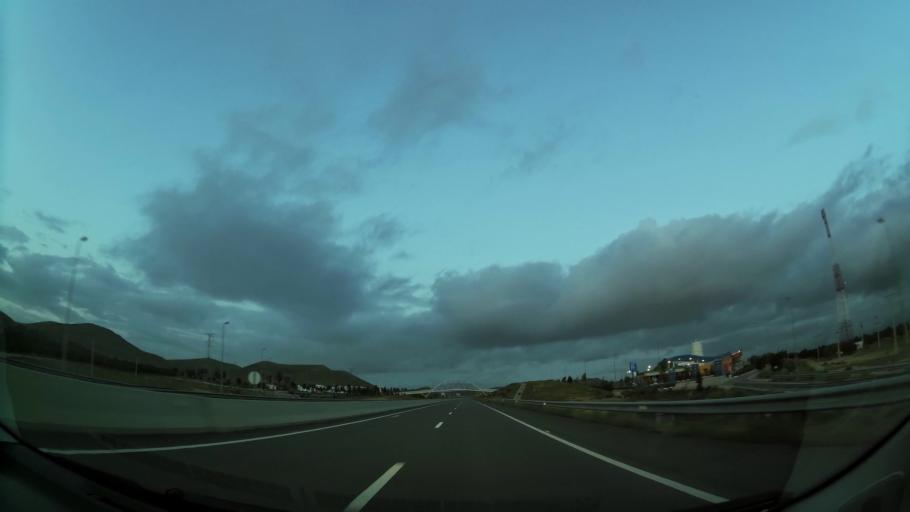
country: MA
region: Oriental
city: El Aioun
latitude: 34.6163
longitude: -2.4419
